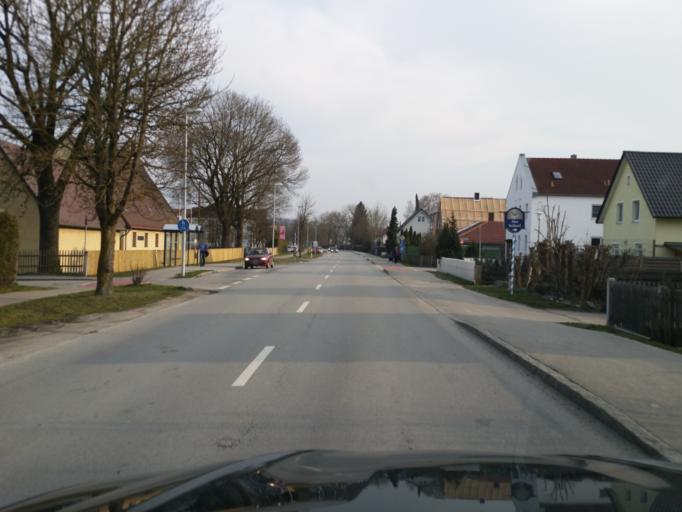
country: DE
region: Bavaria
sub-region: Lower Bavaria
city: Ergolding
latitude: 48.5730
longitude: 12.1746
